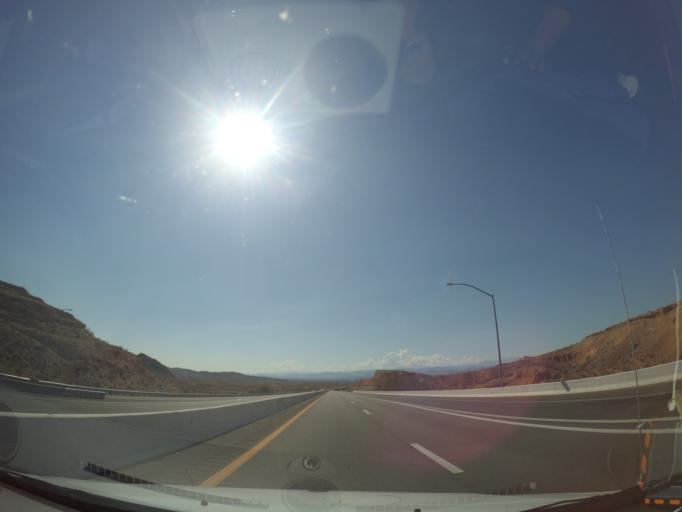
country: US
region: Nevada
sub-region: Clark County
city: Moapa Town
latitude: 36.6693
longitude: -114.5254
